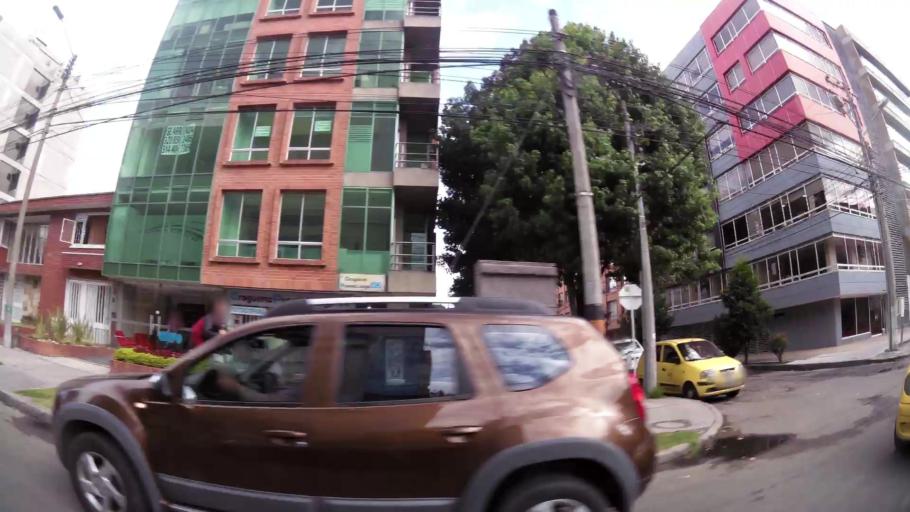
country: CO
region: Bogota D.C.
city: Barrio San Luis
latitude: 4.6945
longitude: -74.0645
